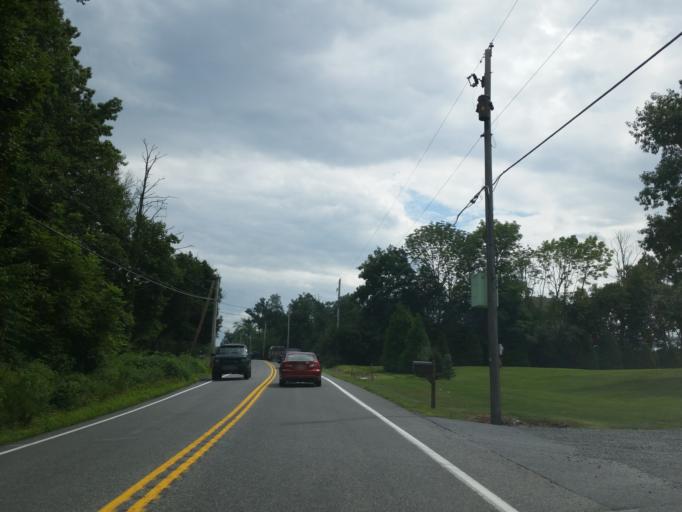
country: US
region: Pennsylvania
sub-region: Lancaster County
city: Swartzville
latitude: 40.2497
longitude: -76.0855
